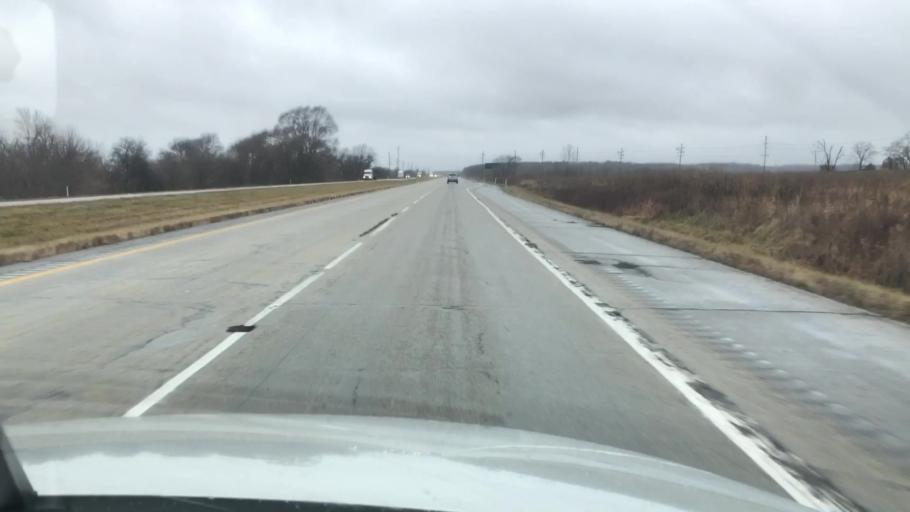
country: US
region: Indiana
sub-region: Starke County
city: Koontz Lake
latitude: 41.3737
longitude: -86.5216
